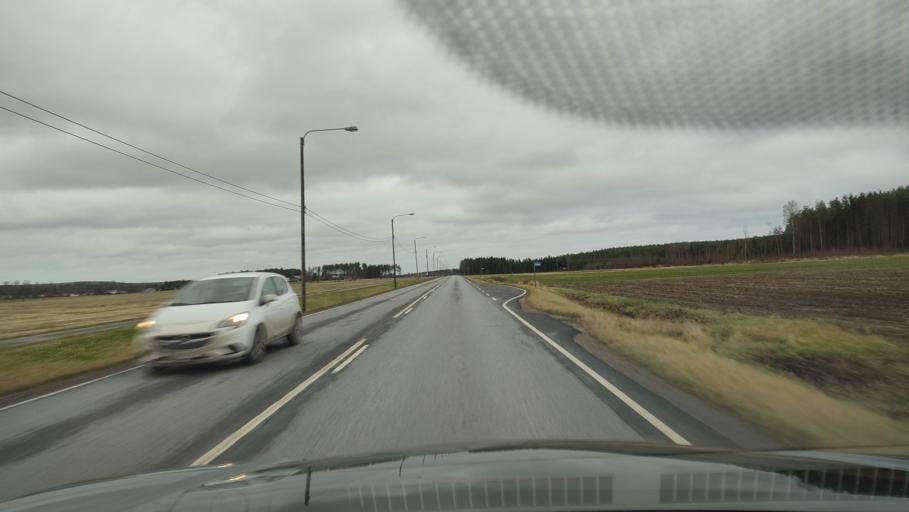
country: FI
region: Southern Ostrobothnia
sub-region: Seinaejoki
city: Kurikka
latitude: 62.5965
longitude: 22.4141
